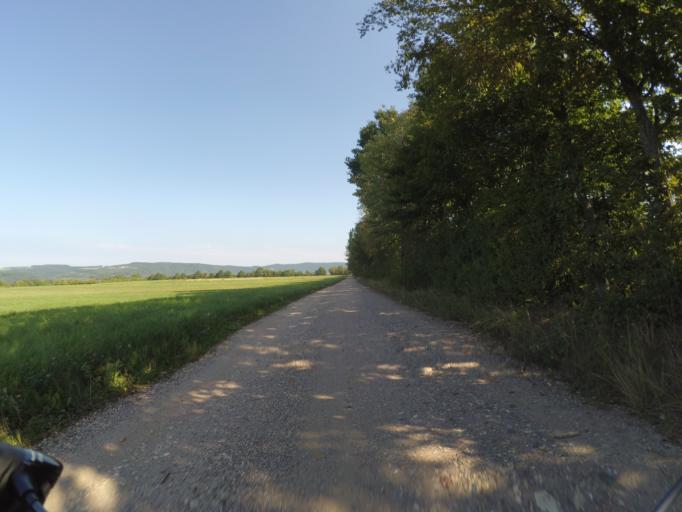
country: DE
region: Rheinland-Pfalz
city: Trittenheim
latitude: 49.8461
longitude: 6.9093
